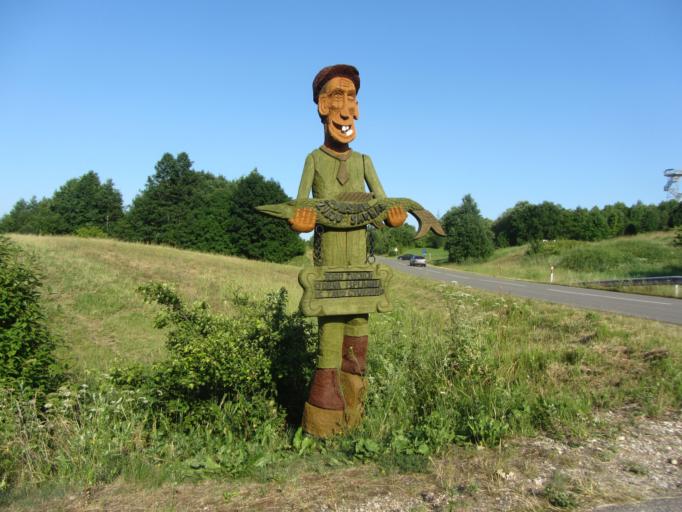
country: LT
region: Utenos apskritis
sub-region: Anyksciai
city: Anyksciai
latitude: 55.4851
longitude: 25.2656
